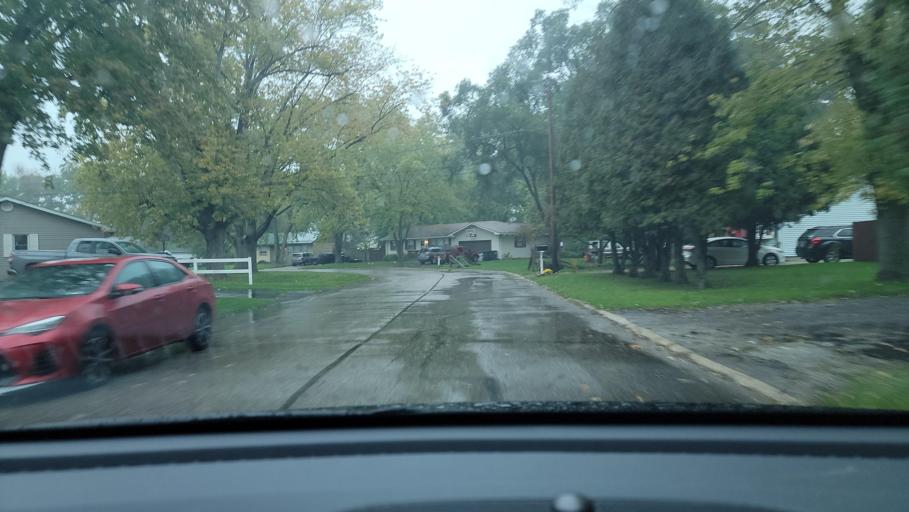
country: US
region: Indiana
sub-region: Porter County
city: Portage
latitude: 41.5856
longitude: -87.1886
